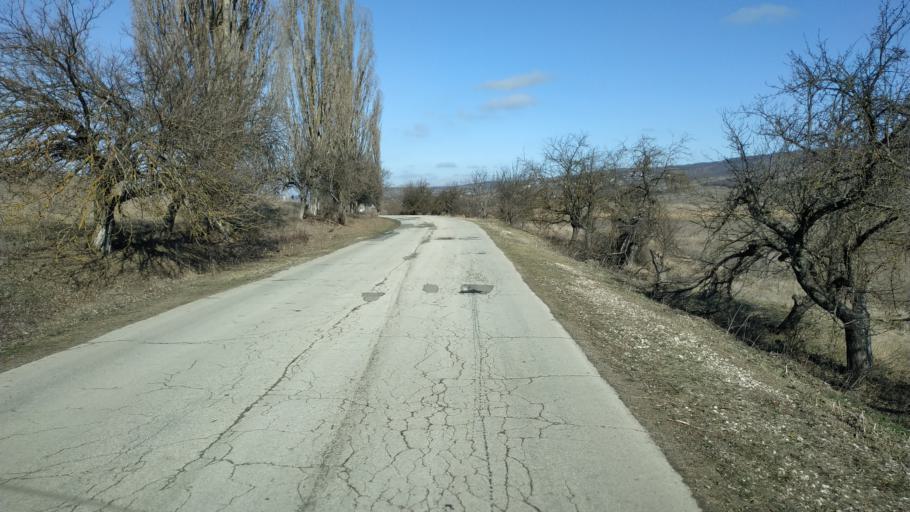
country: MD
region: Straseni
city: Straseni
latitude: 46.9941
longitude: 28.5519
